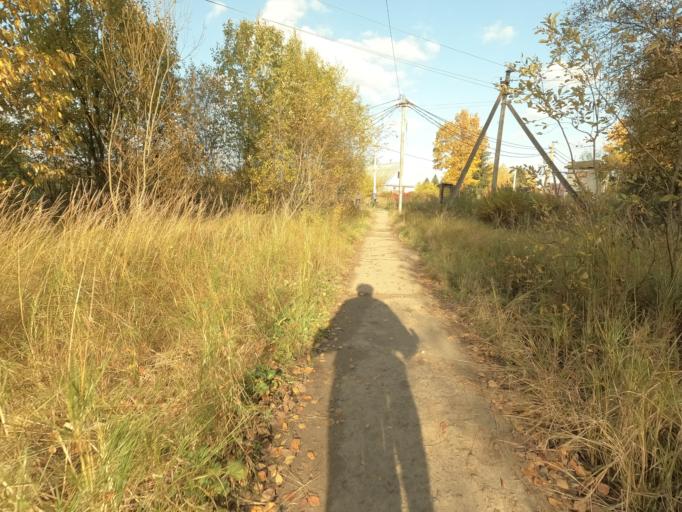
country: RU
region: Leningrad
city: Mga
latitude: 59.7625
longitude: 31.1170
